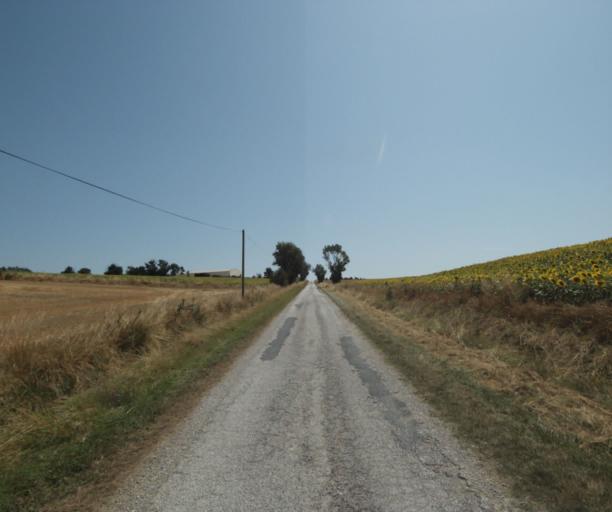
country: FR
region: Midi-Pyrenees
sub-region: Departement de la Haute-Garonne
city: Saint-Felix-Lauragais
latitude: 43.4573
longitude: 1.8536
